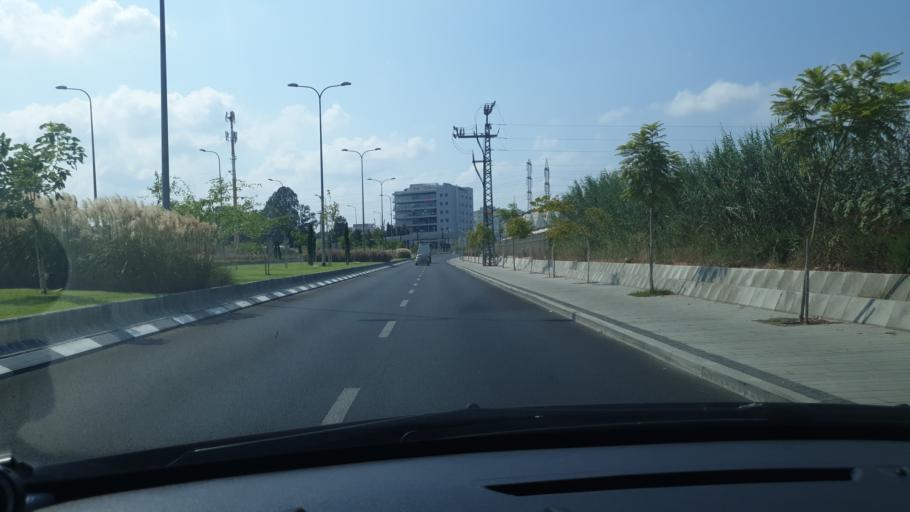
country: IL
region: Haifa
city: Qiryat Bialik
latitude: 32.8153
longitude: 35.0833
